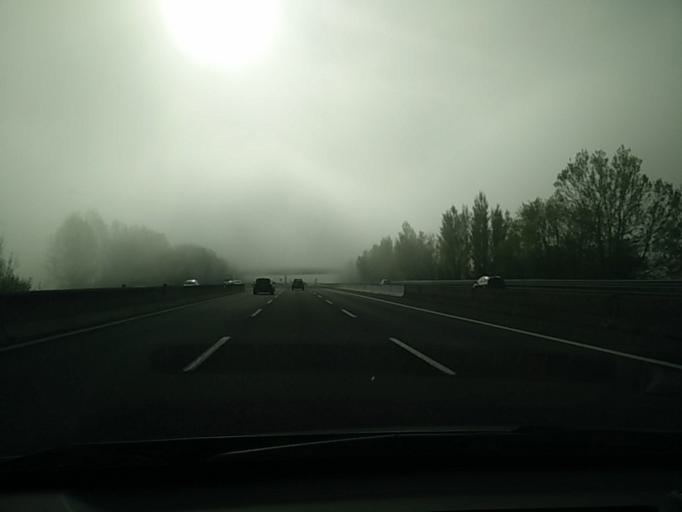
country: IT
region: Emilia-Romagna
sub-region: Provincia di Bologna
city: Ozzano dell'Emilia
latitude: 44.4751
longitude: 11.4622
